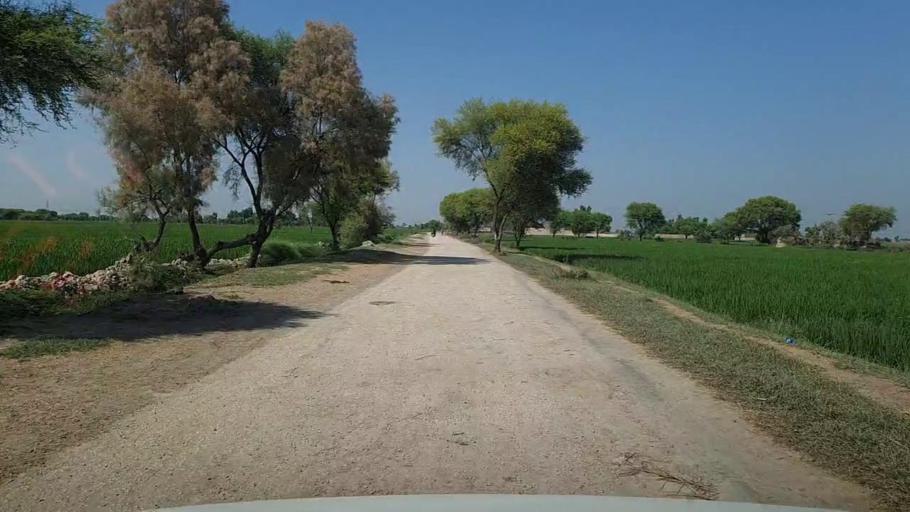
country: PK
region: Sindh
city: Kandhkot
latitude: 28.3265
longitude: 69.3669
